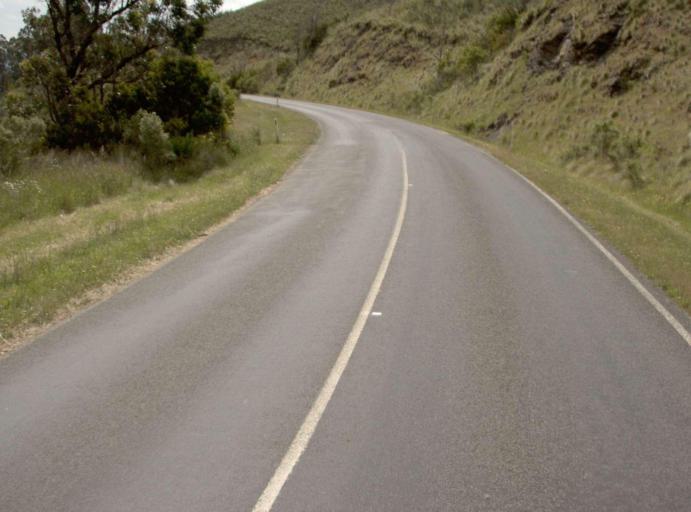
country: AU
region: Victoria
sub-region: Latrobe
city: Traralgon
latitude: -38.3909
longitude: 146.5557
